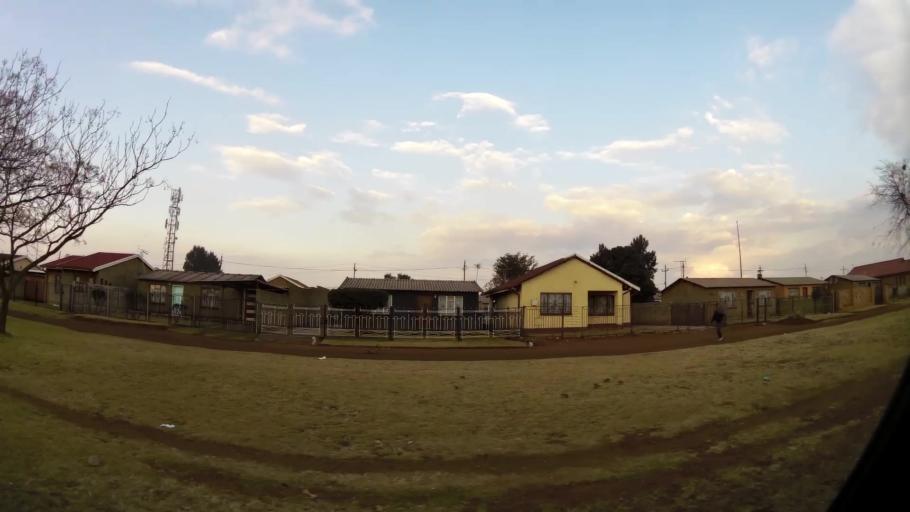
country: ZA
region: Gauteng
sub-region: City of Johannesburg Metropolitan Municipality
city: Orange Farm
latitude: -26.5599
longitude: 27.8382
